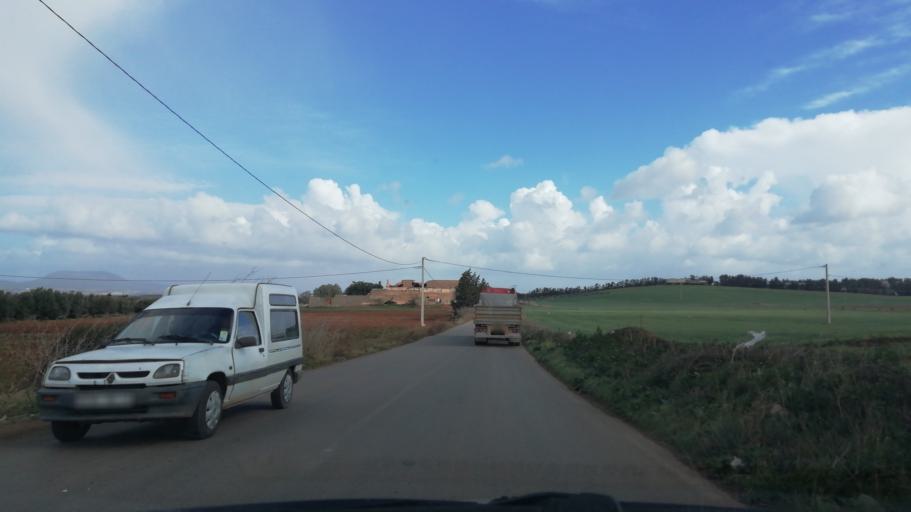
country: DZ
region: Oran
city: Sidi ech Chahmi
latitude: 35.6397
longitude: -0.5188
